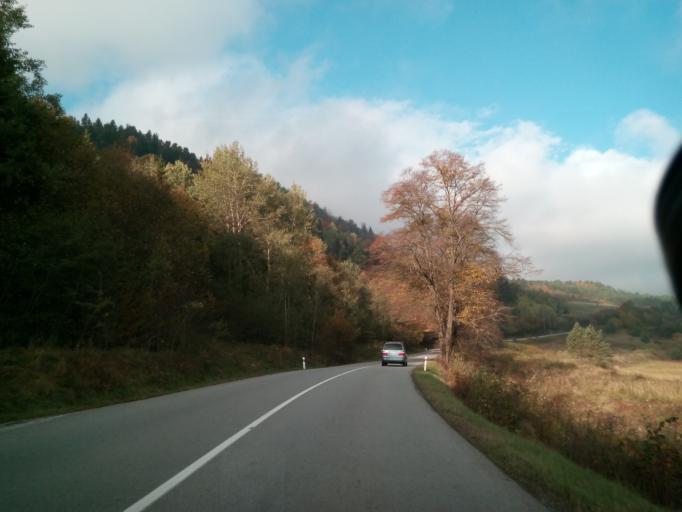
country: SK
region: Kosicky
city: Gelnica
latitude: 48.9121
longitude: 20.9402
